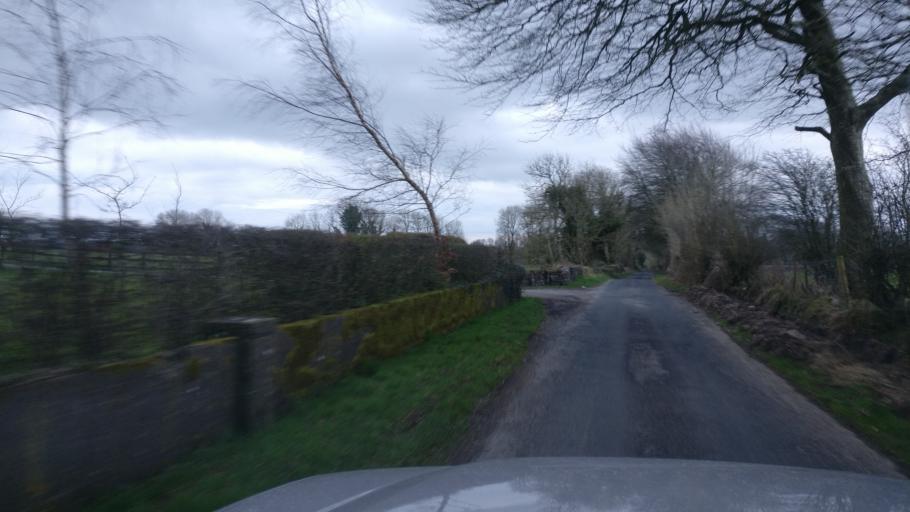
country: IE
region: Connaught
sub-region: County Galway
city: Loughrea
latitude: 53.2632
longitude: -8.4586
